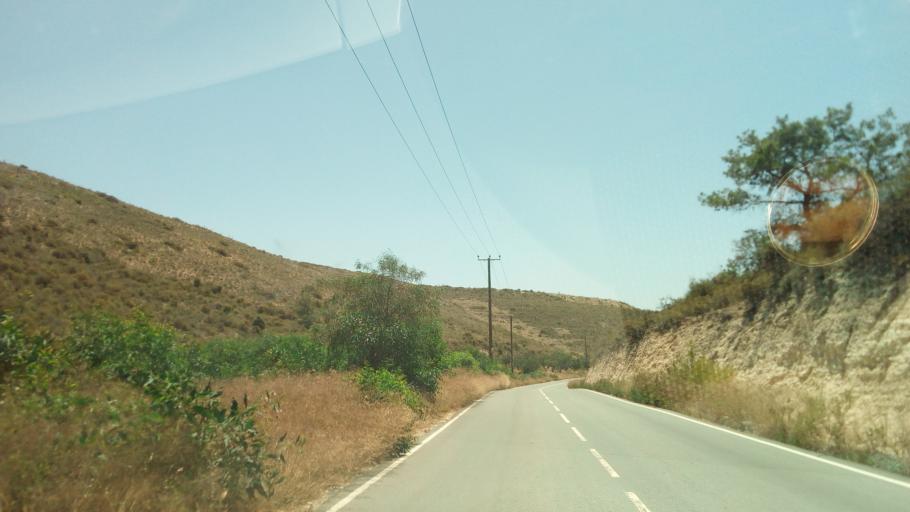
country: CY
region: Limassol
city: Ypsonas
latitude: 34.7397
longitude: 32.9458
